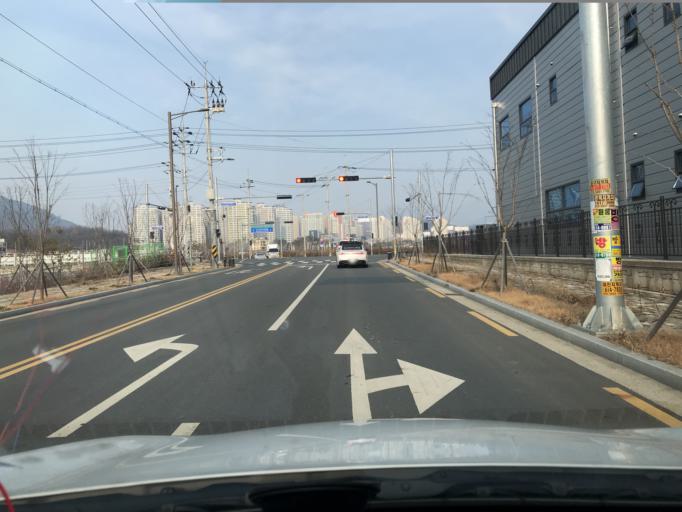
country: KR
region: Gyeongsangnam-do
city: Changnyeong
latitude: 35.6481
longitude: 128.4092
